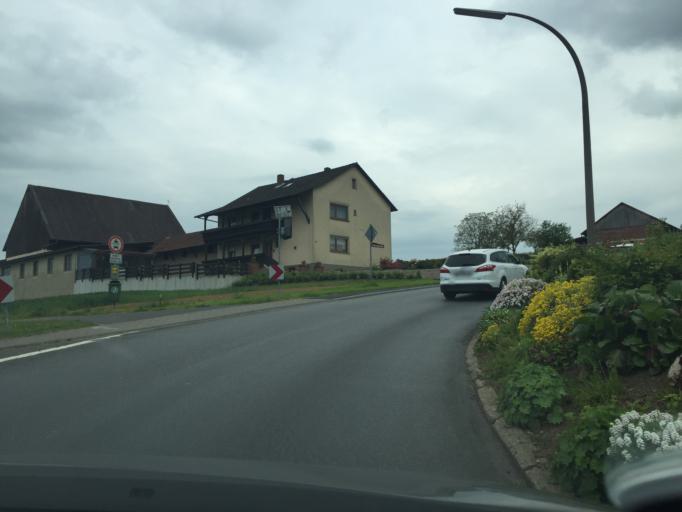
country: DE
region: Bavaria
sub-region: Regierungsbezirk Unterfranken
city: Hosbach
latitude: 50.0268
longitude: 9.1894
